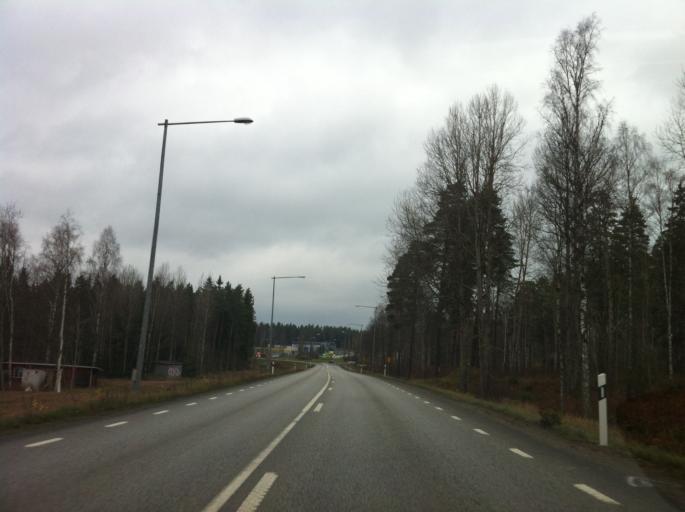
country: SE
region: Joenkoeping
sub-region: Vetlanda Kommun
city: Vetlanda
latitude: 57.4189
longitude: 15.0588
